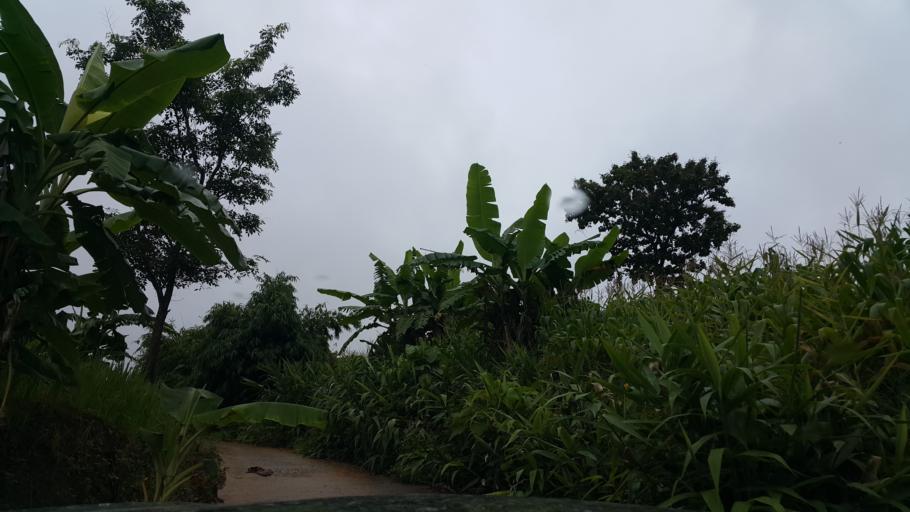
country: TH
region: Phayao
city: Chiang Kham
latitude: 19.4984
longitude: 100.4660
